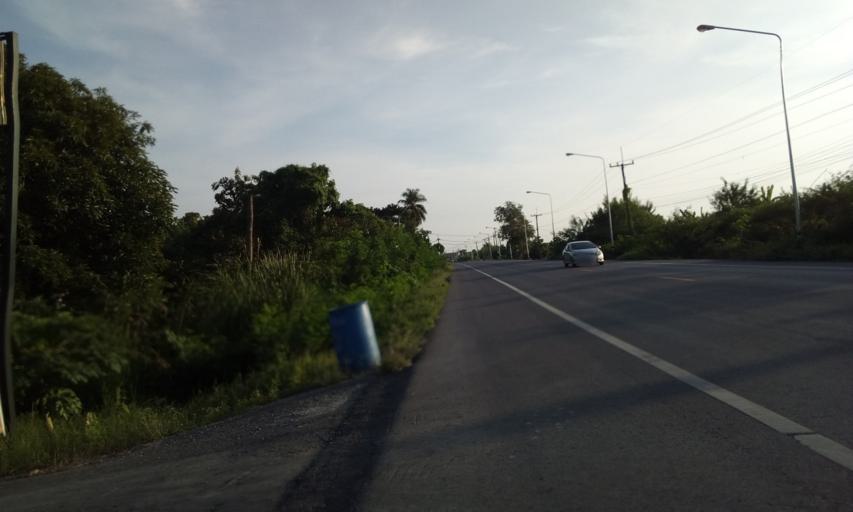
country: TH
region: Pathum Thani
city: Ban Rangsit
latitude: 14.0401
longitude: 100.8444
